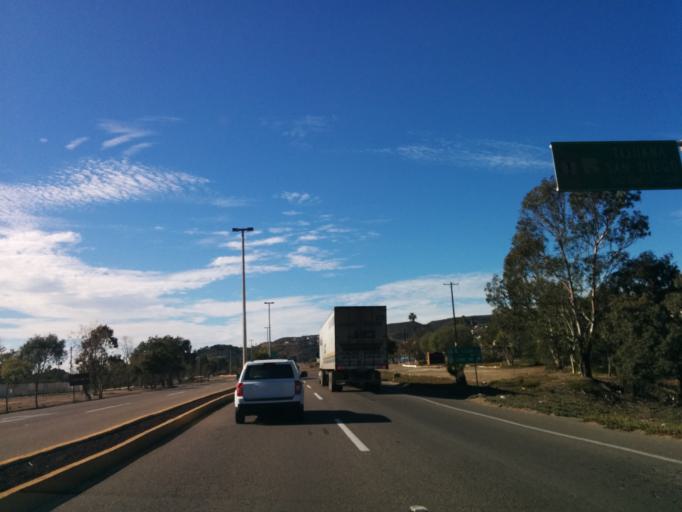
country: MX
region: Baja California
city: El Sauzal
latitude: 31.9038
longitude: -116.7232
